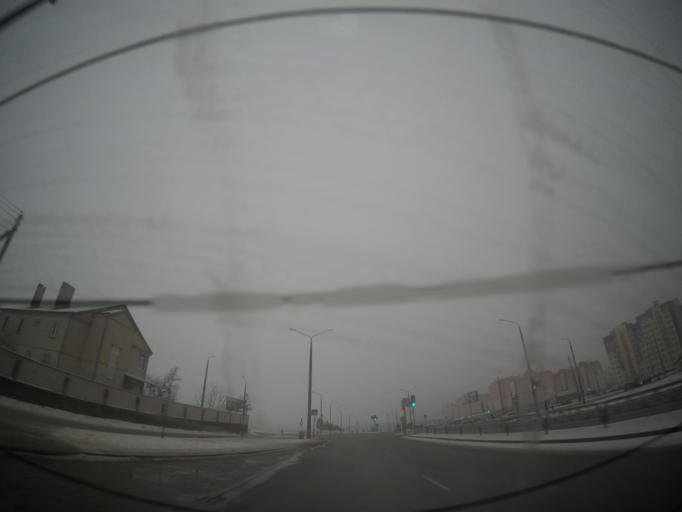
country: BY
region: Grodnenskaya
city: Hrodna
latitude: 53.6248
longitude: 23.8119
